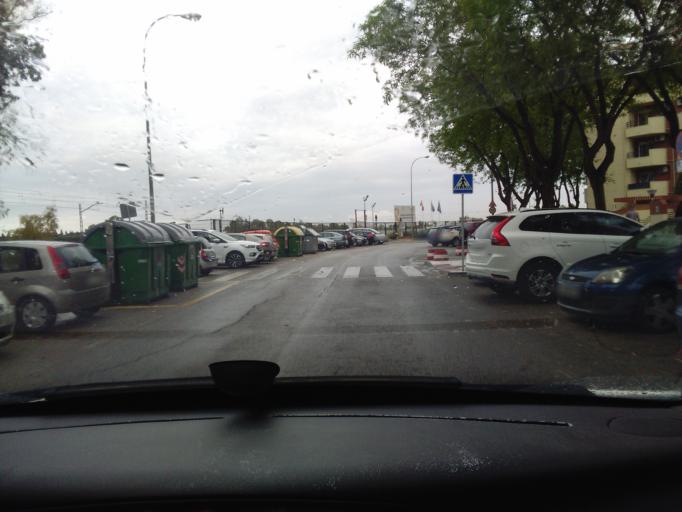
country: ES
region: Andalusia
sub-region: Provincia de Sevilla
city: Sevilla
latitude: 37.4019
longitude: -5.9363
